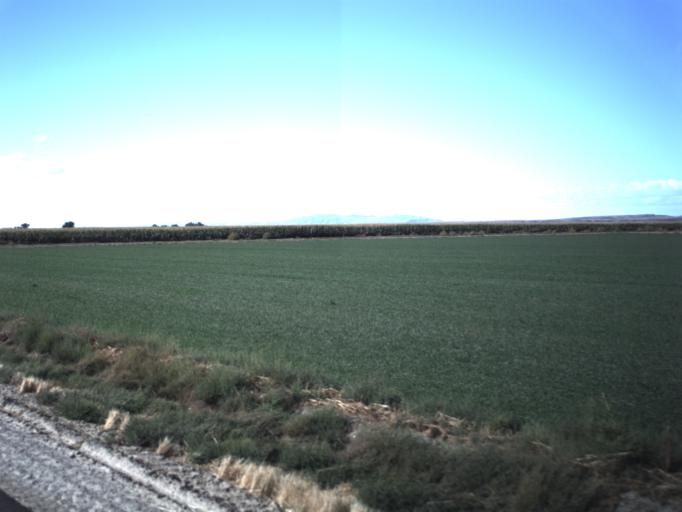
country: US
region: Utah
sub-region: Millard County
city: Delta
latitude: 39.2771
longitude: -112.6530
